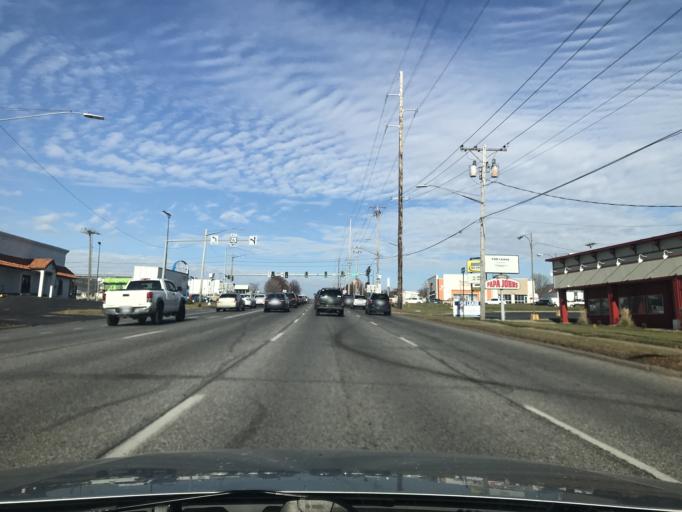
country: US
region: Iowa
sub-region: Scott County
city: Davenport
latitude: 41.5592
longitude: -90.5683
